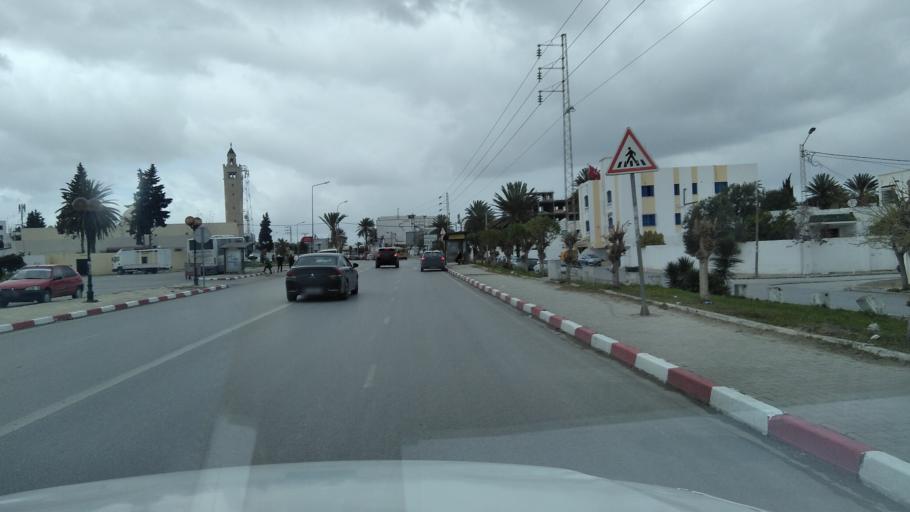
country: TN
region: Bin 'Arus
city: Ben Arous
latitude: 36.7506
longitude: 10.2264
